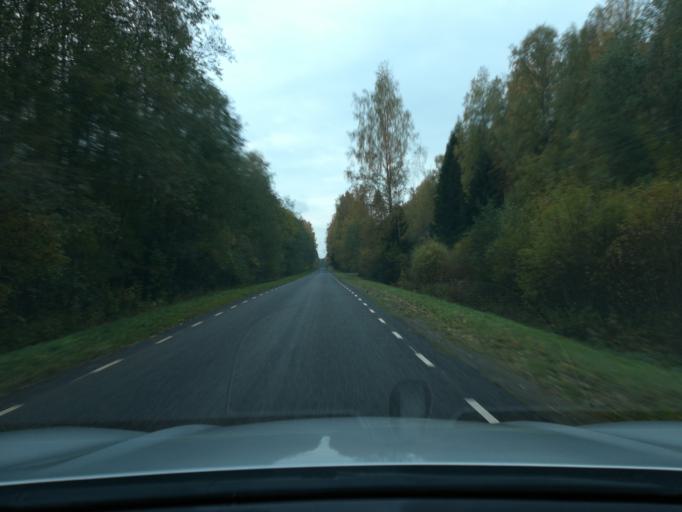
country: EE
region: Ida-Virumaa
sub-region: Johvi vald
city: Johvi
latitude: 59.0422
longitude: 27.3952
